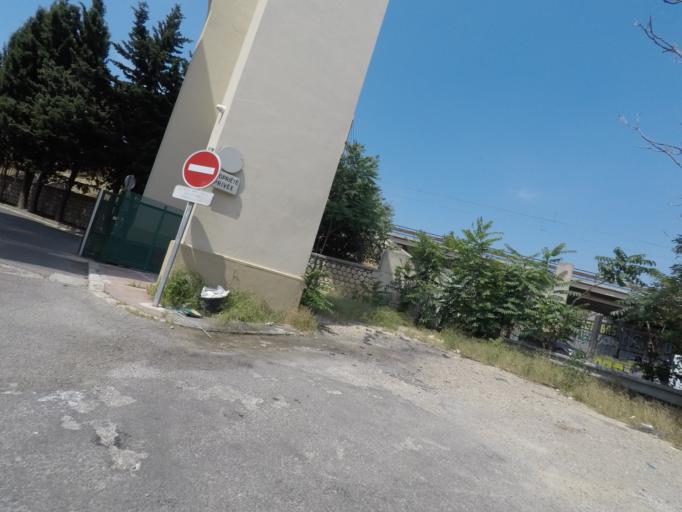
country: FR
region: Provence-Alpes-Cote d'Azur
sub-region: Departement des Bouches-du-Rhone
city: Marseille 10
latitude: 43.2845
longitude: 5.4074
